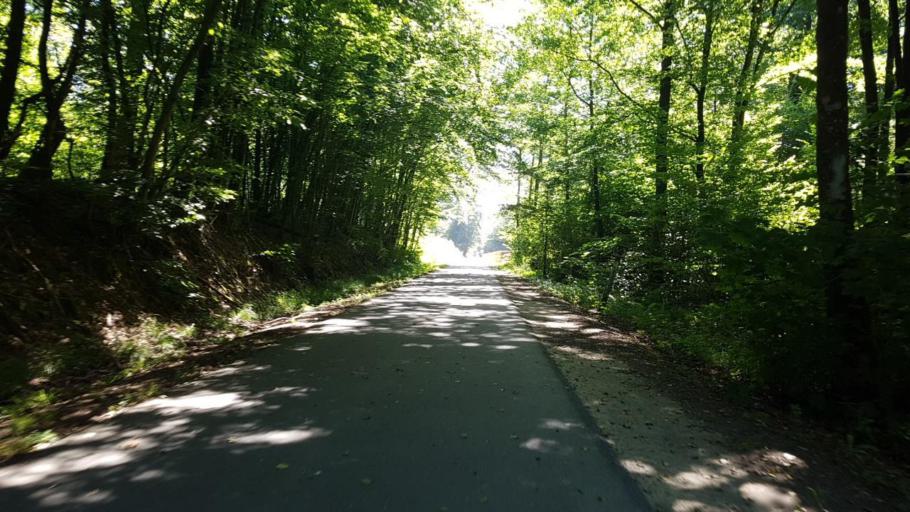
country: BE
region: Wallonia
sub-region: Province du Hainaut
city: Momignies
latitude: 50.0264
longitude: 4.1960
